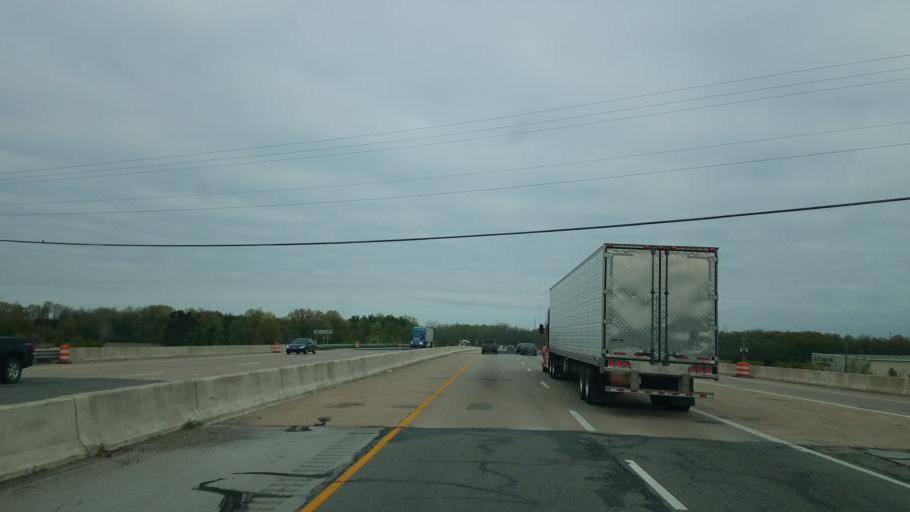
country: US
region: Indiana
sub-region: Allen County
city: Fort Wayne
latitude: 41.1616
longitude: -85.0694
